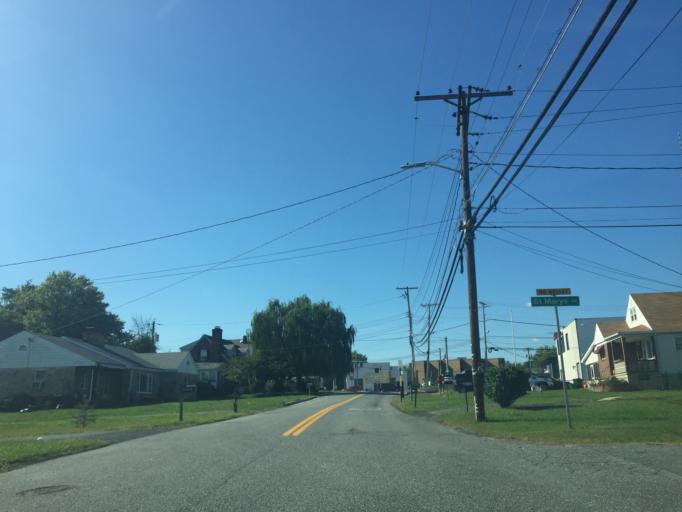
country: US
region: Maryland
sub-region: Baltimore County
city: Overlea
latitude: 39.3712
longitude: -76.5101
